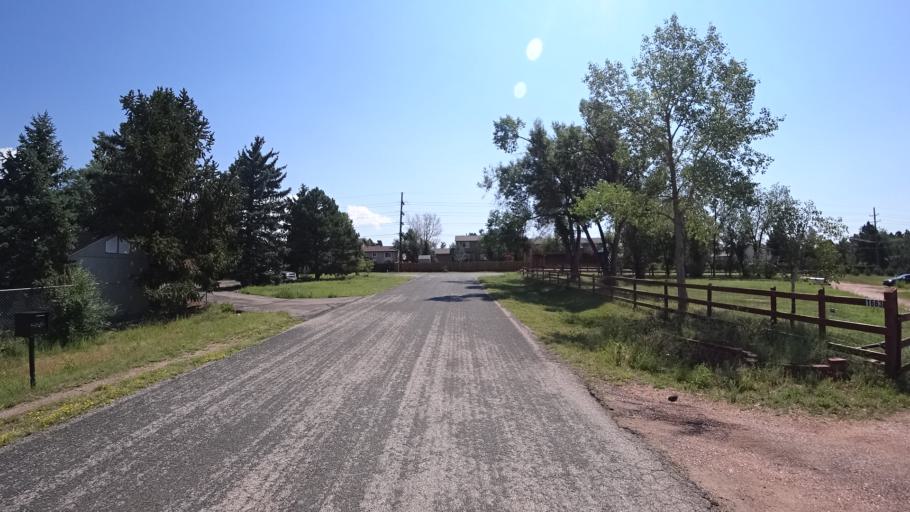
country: US
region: Colorado
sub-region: El Paso County
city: Air Force Academy
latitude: 38.9412
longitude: -104.7945
